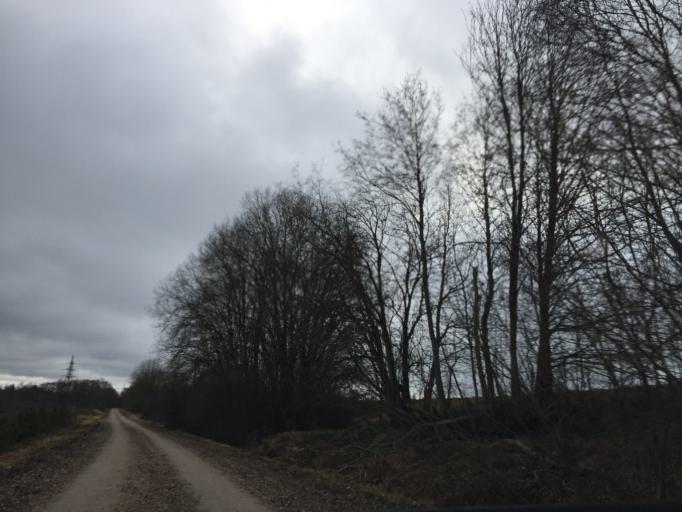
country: LV
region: Broceni
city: Broceni
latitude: 56.6772
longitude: 22.5576
